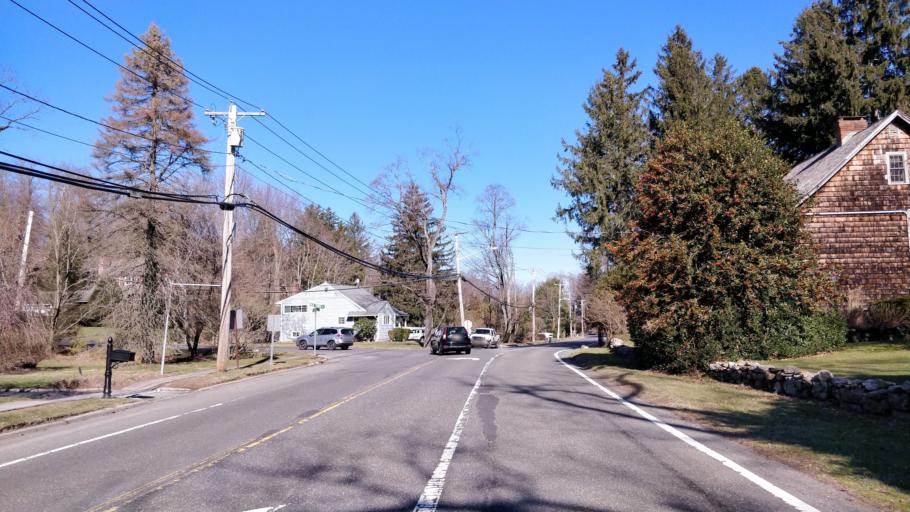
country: US
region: New York
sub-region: Suffolk County
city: Setauket-East Setauket
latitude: 40.9366
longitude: -73.0995
